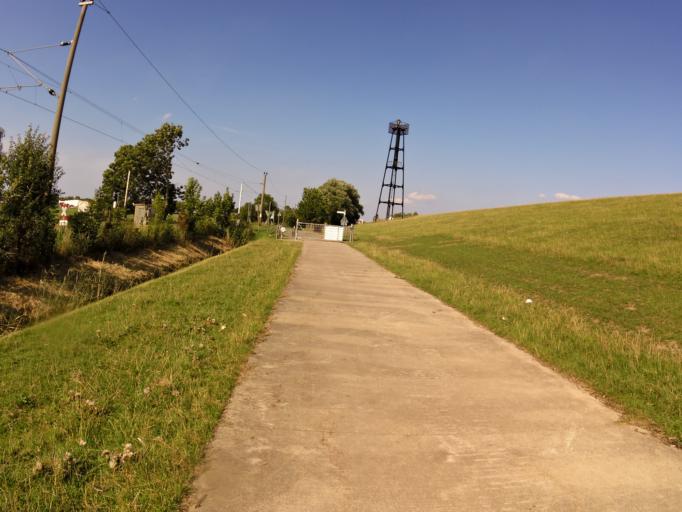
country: DE
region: Lower Saxony
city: Nordenham
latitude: 53.4643
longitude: 8.4757
